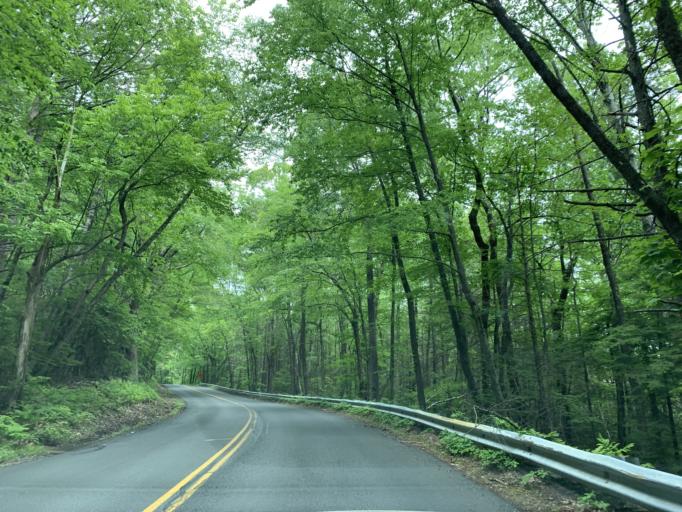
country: US
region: Massachusetts
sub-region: Hampshire County
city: Southampton
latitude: 42.1950
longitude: -72.7857
